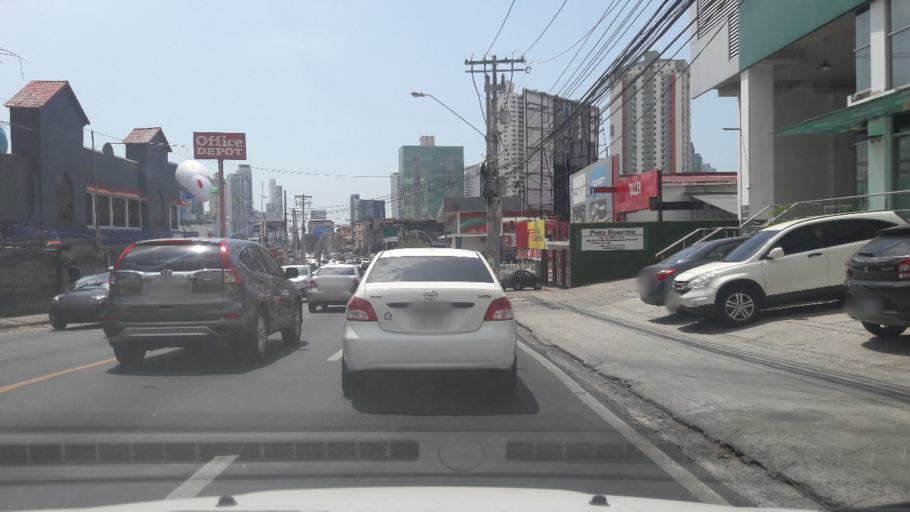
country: PA
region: Panama
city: Panama
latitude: 8.9919
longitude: -79.5219
